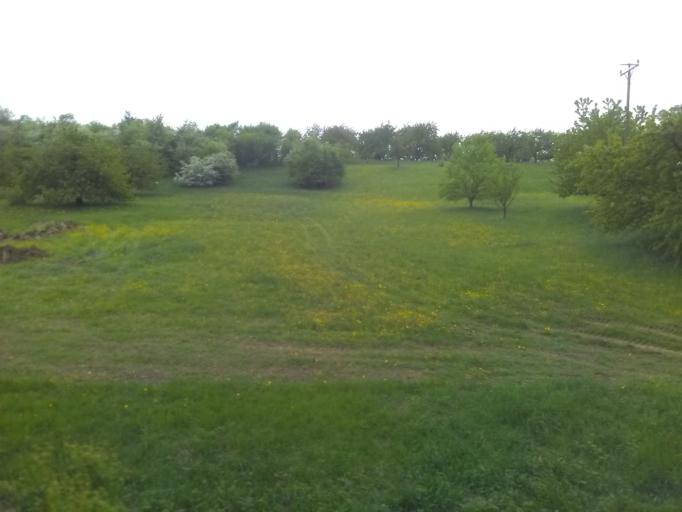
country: DE
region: Bavaria
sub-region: Regierungsbezirk Mittelfranken
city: Kalchreuth
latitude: 49.5610
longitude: 11.1524
